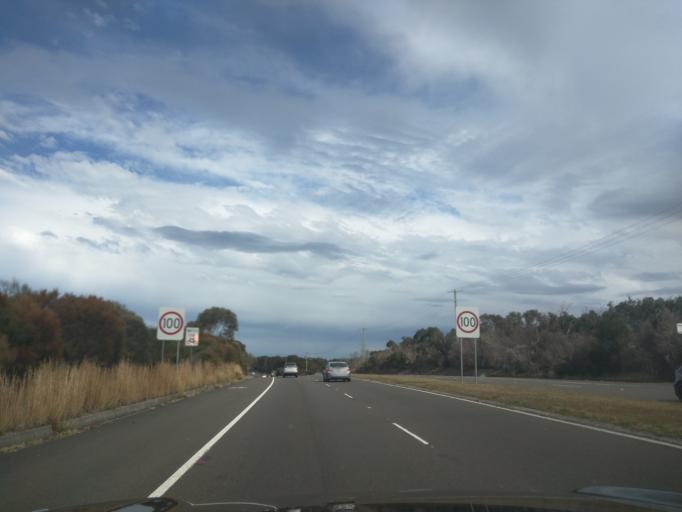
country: AU
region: New South Wales
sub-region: Sutherland Shire
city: Heathcote
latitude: -34.0990
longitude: 150.9965
